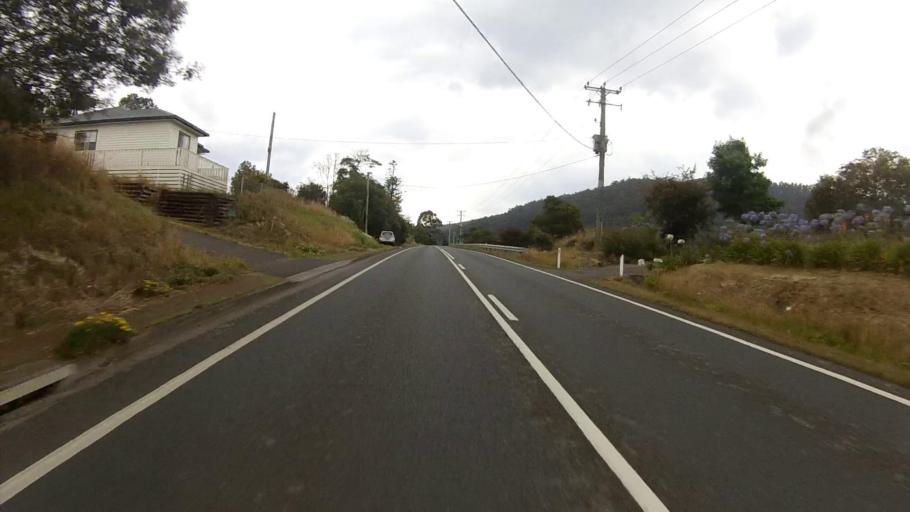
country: AU
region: Tasmania
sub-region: Huon Valley
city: Cygnet
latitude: -43.1460
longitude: 147.0657
